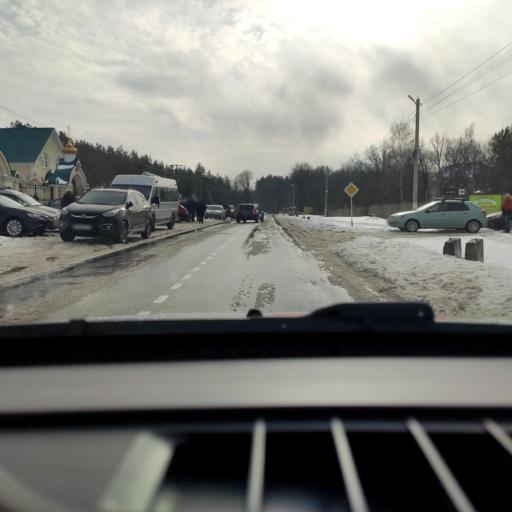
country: RU
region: Voronezj
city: Podgornoye
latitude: 51.7887
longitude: 39.1459
